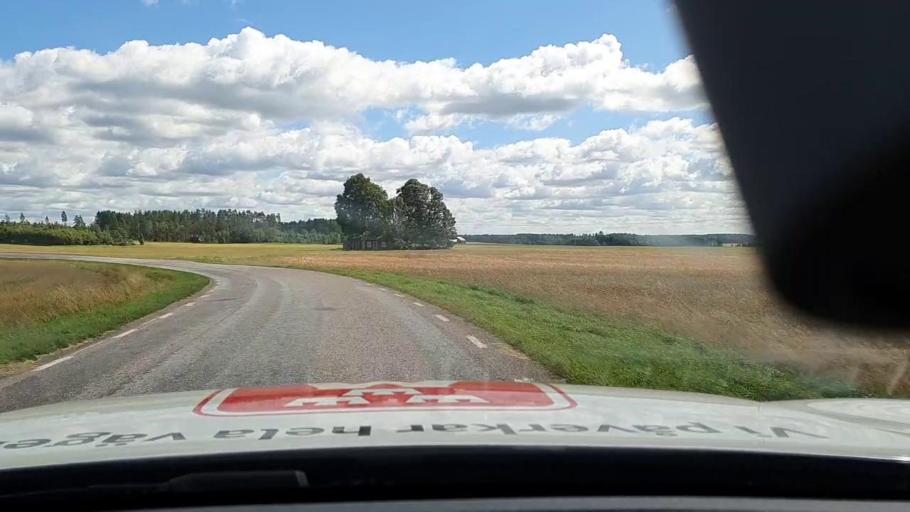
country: SE
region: Vaestra Goetaland
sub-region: Toreboda Kommun
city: Toereboda
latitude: 58.5836
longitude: 14.1149
